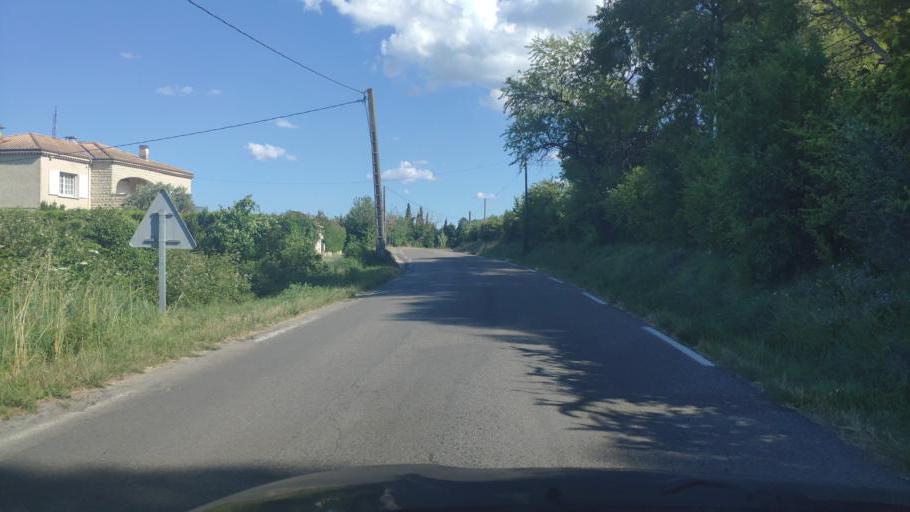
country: FR
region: Provence-Alpes-Cote d'Azur
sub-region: Departement du Vaucluse
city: Entraigues-sur-la-Sorgue
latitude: 43.9901
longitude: 4.9139
